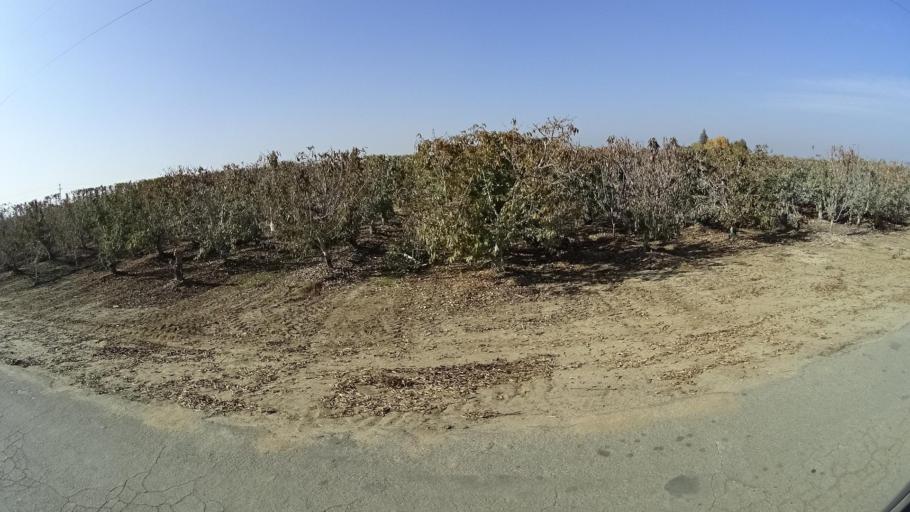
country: US
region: California
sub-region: Kern County
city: McFarland
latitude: 35.6031
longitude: -119.1866
